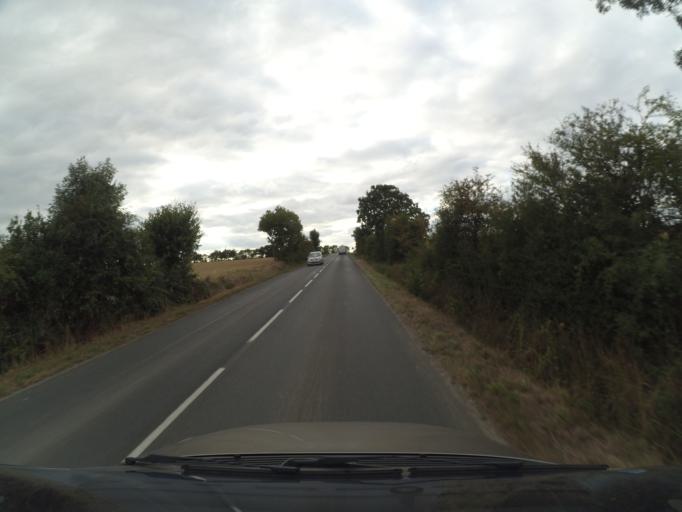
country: FR
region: Pays de la Loire
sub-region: Departement de la Vendee
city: Saint-Andre-Treize-Voies
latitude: 46.9237
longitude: -1.3960
